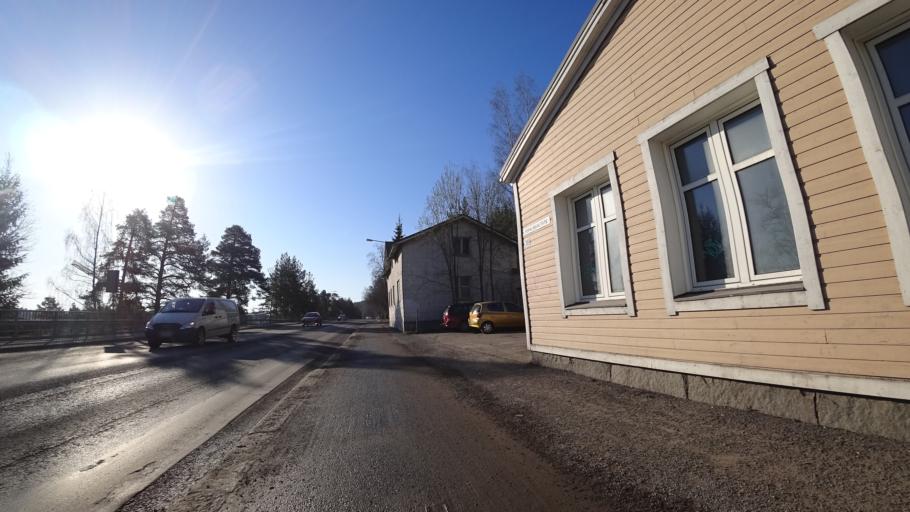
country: FI
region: Pirkanmaa
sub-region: Tampere
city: Tampere
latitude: 61.5018
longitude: 23.7212
